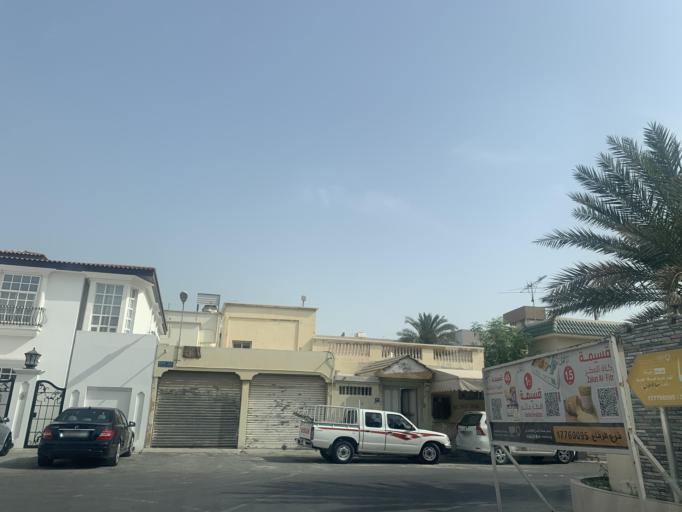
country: BH
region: Northern
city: Ar Rifa'
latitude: 26.1320
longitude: 50.5583
